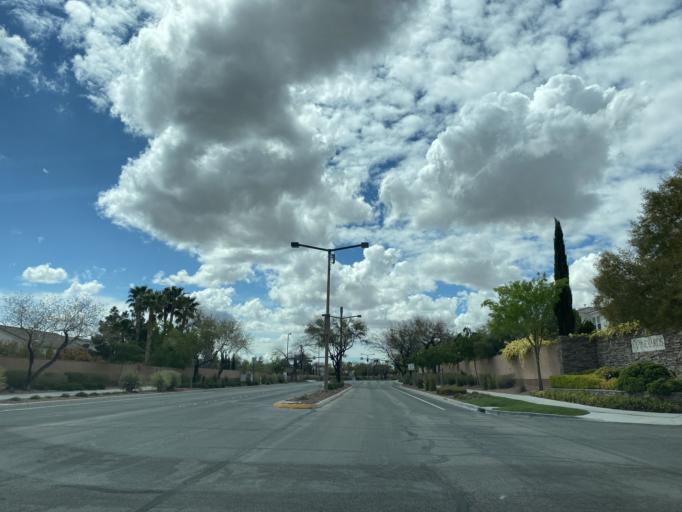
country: US
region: Nevada
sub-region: Clark County
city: Summerlin South
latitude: 36.1870
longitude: -115.3292
